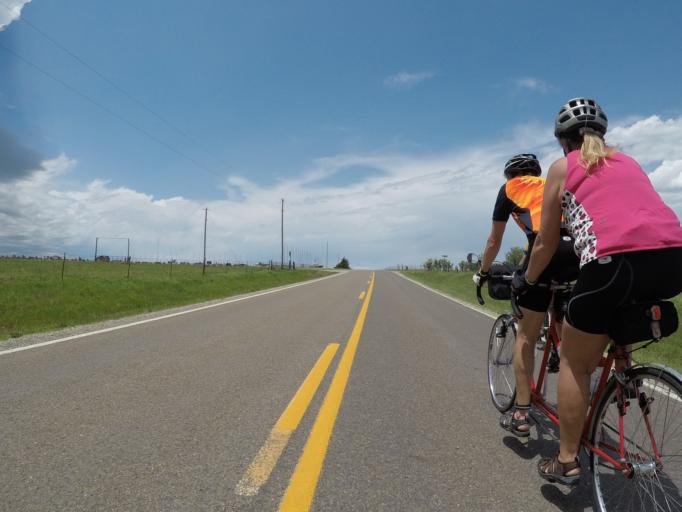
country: US
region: Kansas
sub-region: Morris County
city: Council Grove
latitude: 38.8551
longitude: -96.4634
